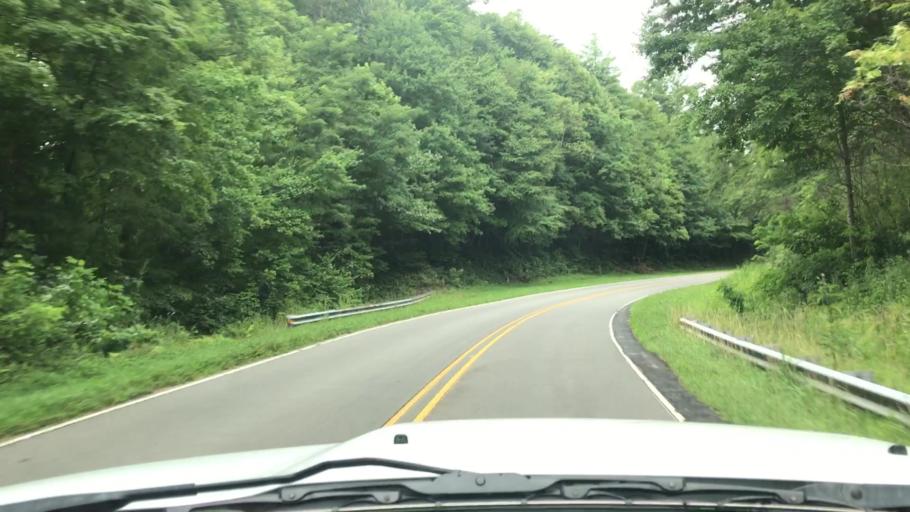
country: US
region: North Carolina
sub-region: Graham County
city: Robbinsville
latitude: 35.3683
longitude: -83.8644
